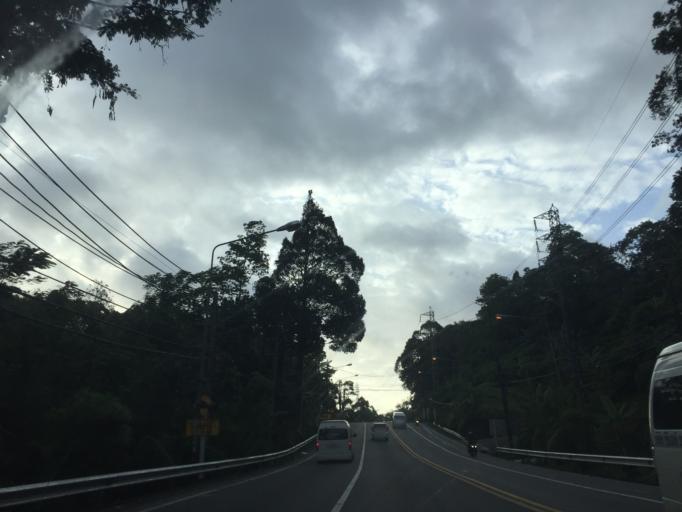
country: TH
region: Phuket
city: Kathu
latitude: 7.9029
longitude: 98.3196
